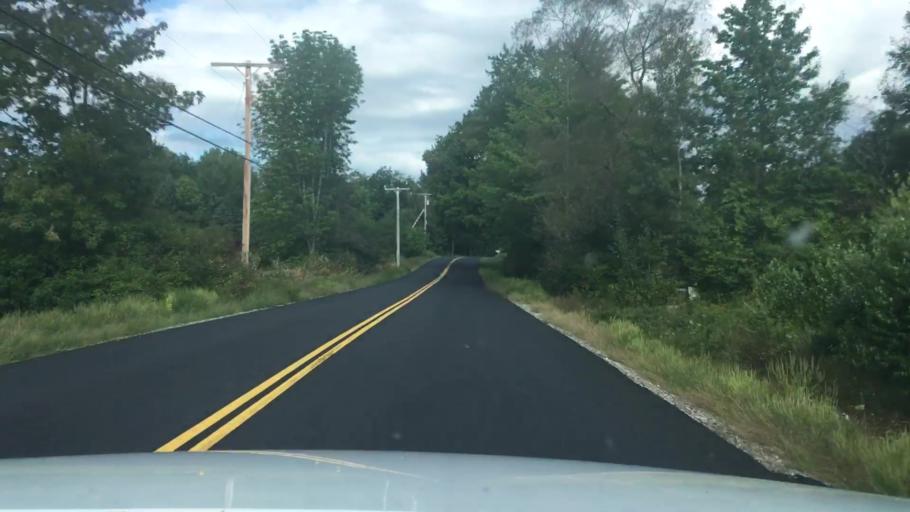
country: US
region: Maine
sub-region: Androscoggin County
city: Lisbon Falls
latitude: 44.0411
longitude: -70.0395
